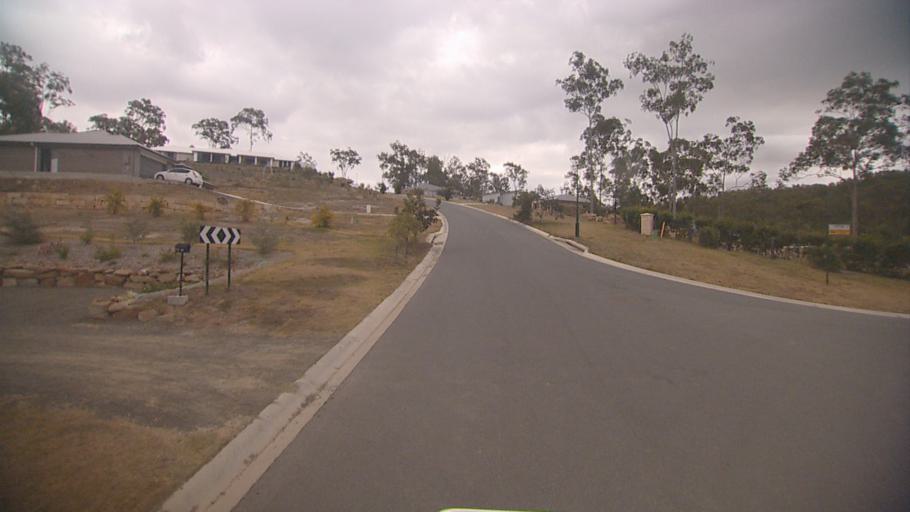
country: AU
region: Queensland
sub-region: Logan
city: Cedar Vale
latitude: -27.8607
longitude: 153.0780
